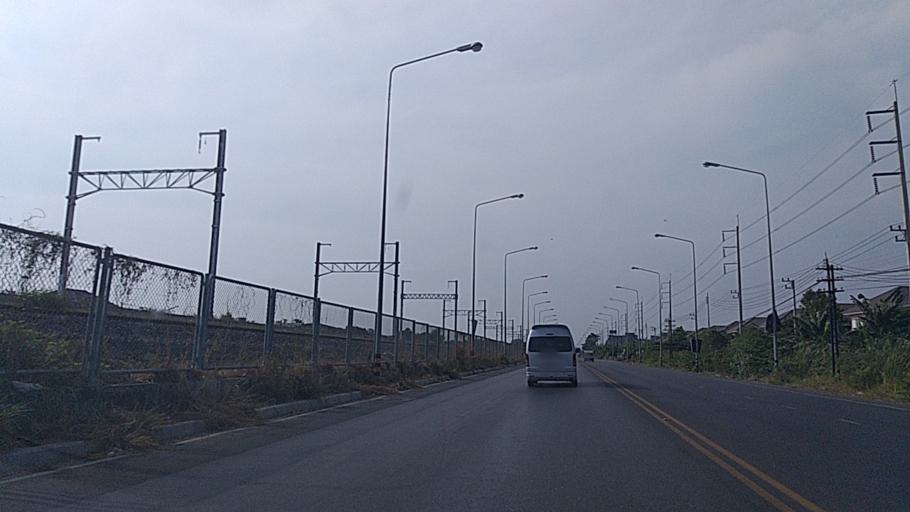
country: TH
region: Phra Nakhon Si Ayutthaya
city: Ban Bang Kadi Pathum Thani
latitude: 13.9791
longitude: 100.6034
